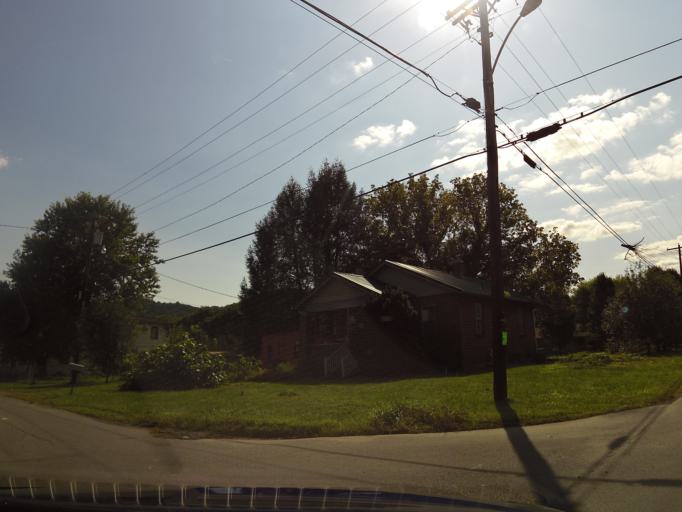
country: US
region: Kentucky
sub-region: Bell County
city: Middlesboro
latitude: 36.6036
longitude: -83.7297
